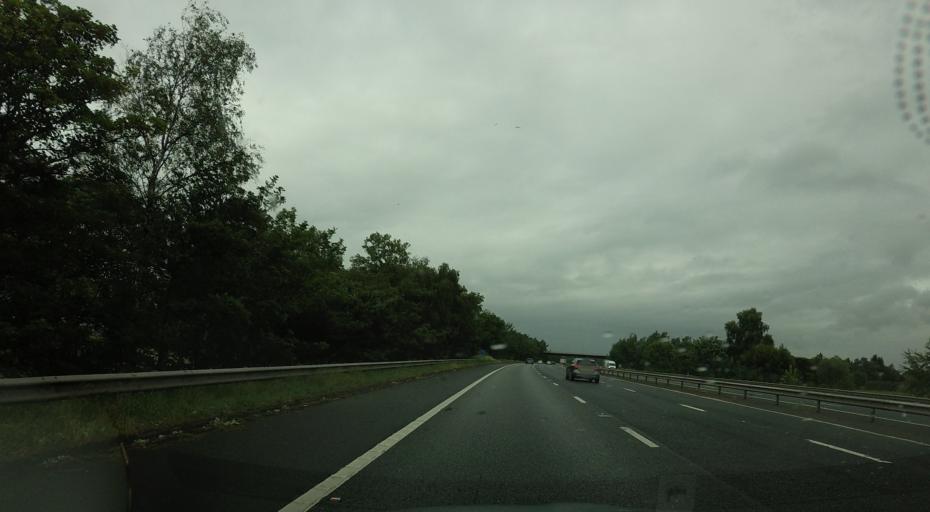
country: GB
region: England
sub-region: Cumbria
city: Scotby
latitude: 54.9108
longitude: -2.8981
